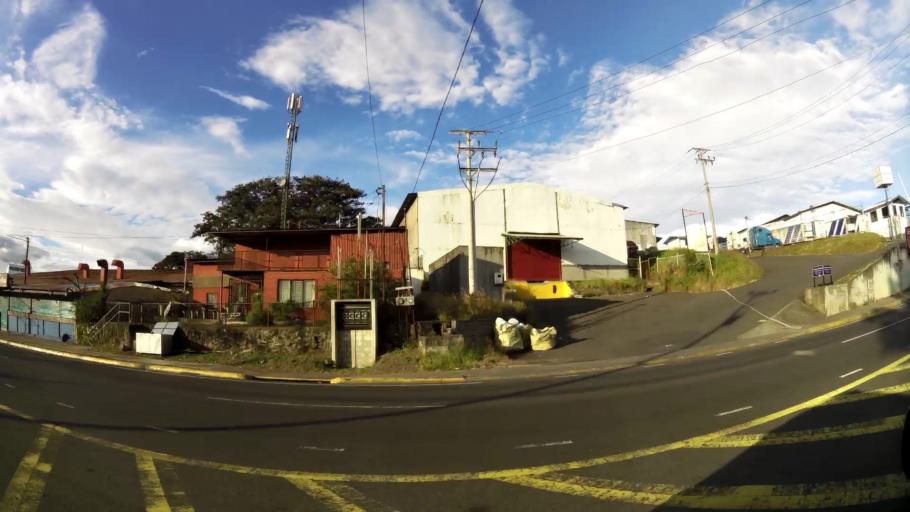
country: CR
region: Heredia
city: Llorente
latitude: 10.0035
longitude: -84.1688
